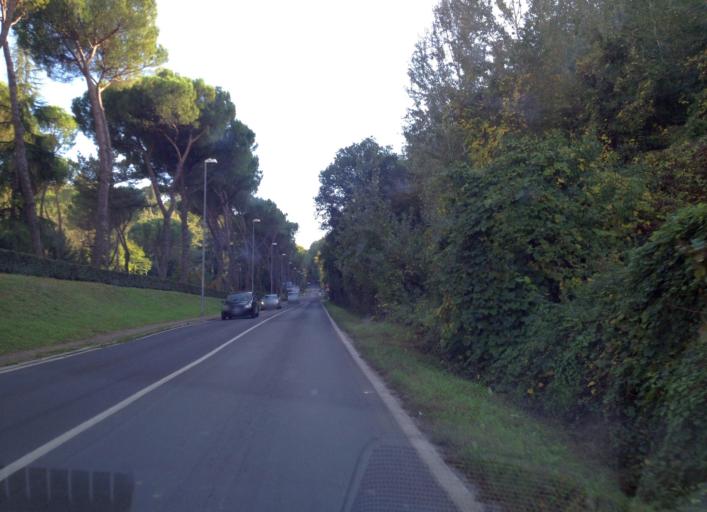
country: IT
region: Tuscany
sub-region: Provincia di Siena
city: Poggibonsi
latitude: 43.4649
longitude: 11.1450
